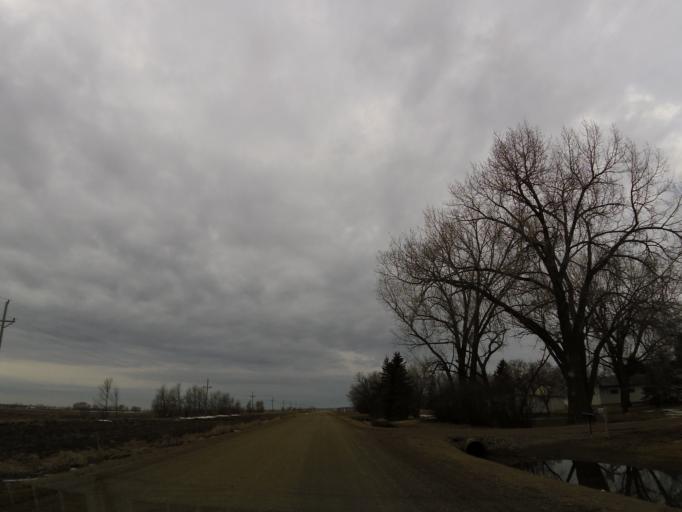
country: US
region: North Dakota
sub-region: Walsh County
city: Grafton
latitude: 48.4198
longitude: -97.4324
